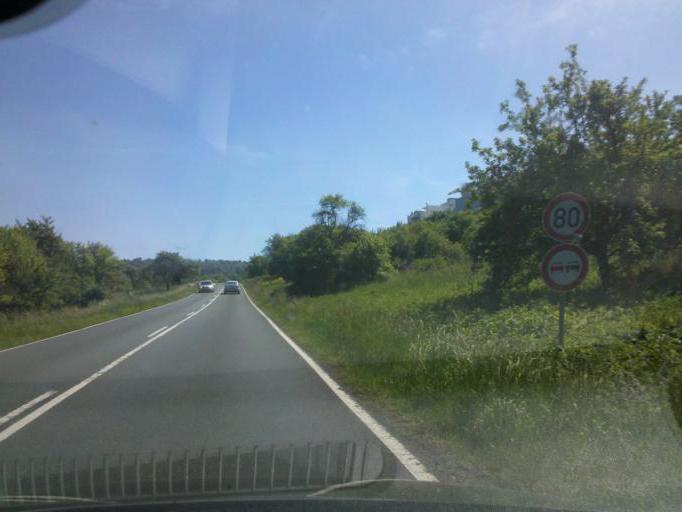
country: DE
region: Hesse
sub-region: Regierungsbezirk Giessen
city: Haiger
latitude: 50.7263
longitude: 8.1885
